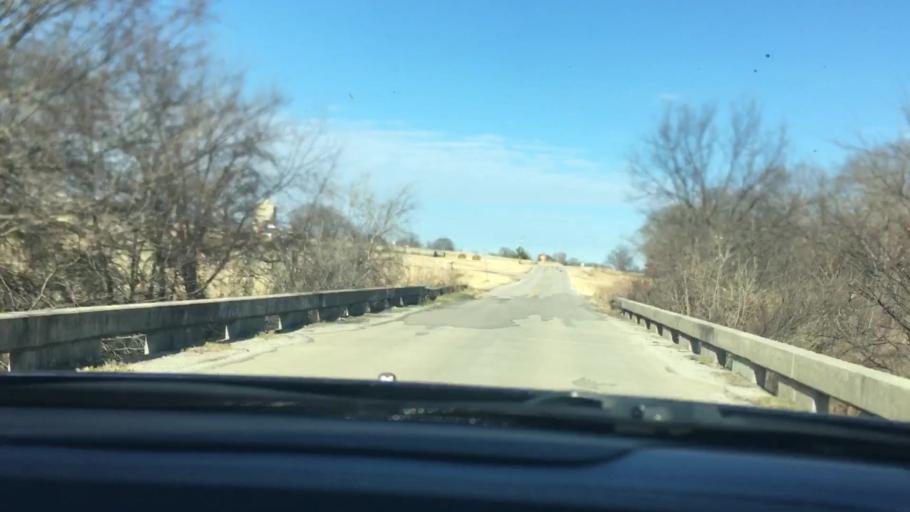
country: US
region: Oklahoma
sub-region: Garvin County
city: Wynnewood
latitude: 34.7229
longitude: -97.1253
